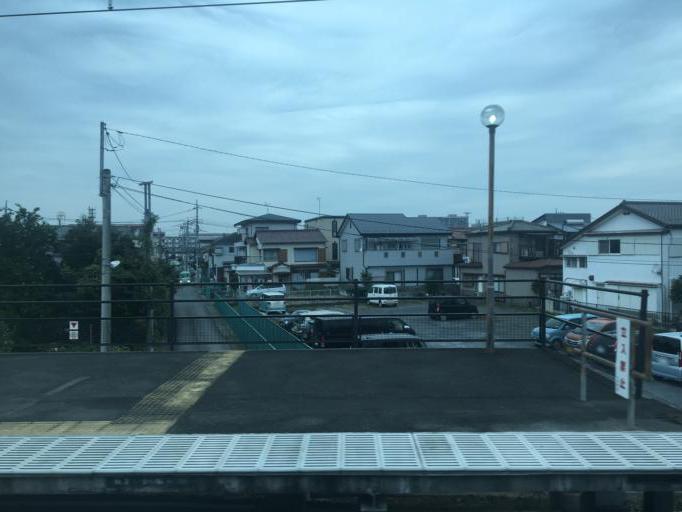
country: JP
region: Saitama
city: Kamifukuoka
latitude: 35.9175
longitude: 139.5659
